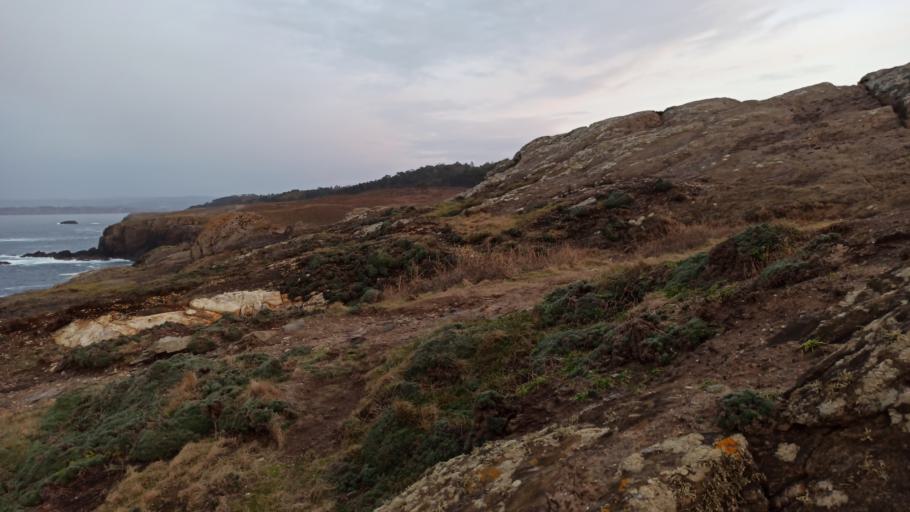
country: ES
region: Galicia
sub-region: Provincia da Coruna
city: A Coruna
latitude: 43.3961
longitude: -8.3498
